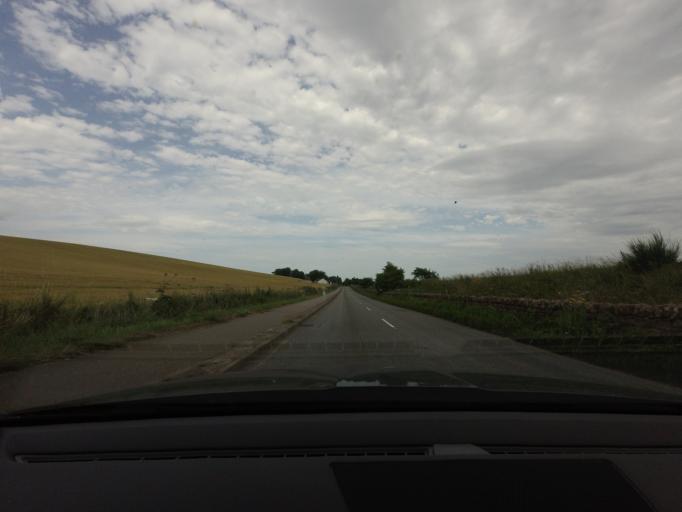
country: GB
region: Scotland
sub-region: Highland
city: Alness
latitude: 57.6871
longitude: -4.2830
